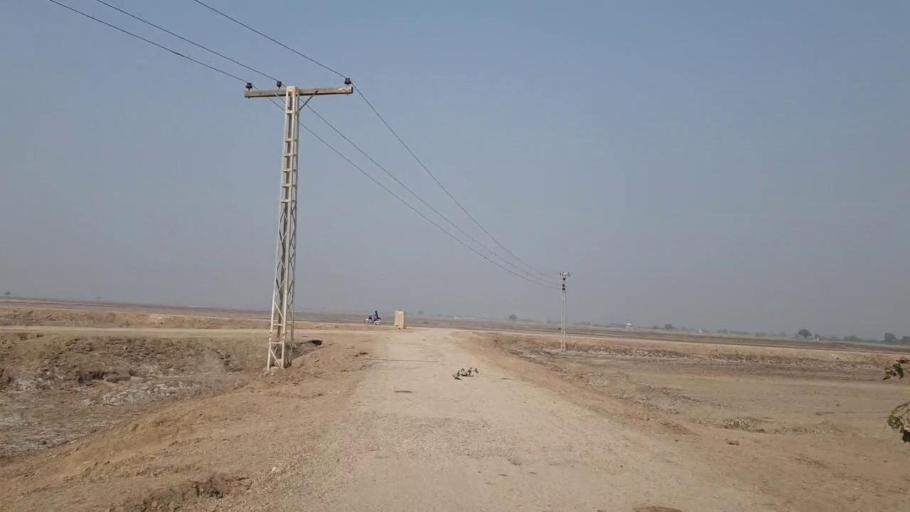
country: PK
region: Sindh
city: Bhan
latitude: 26.4479
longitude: 67.7139
